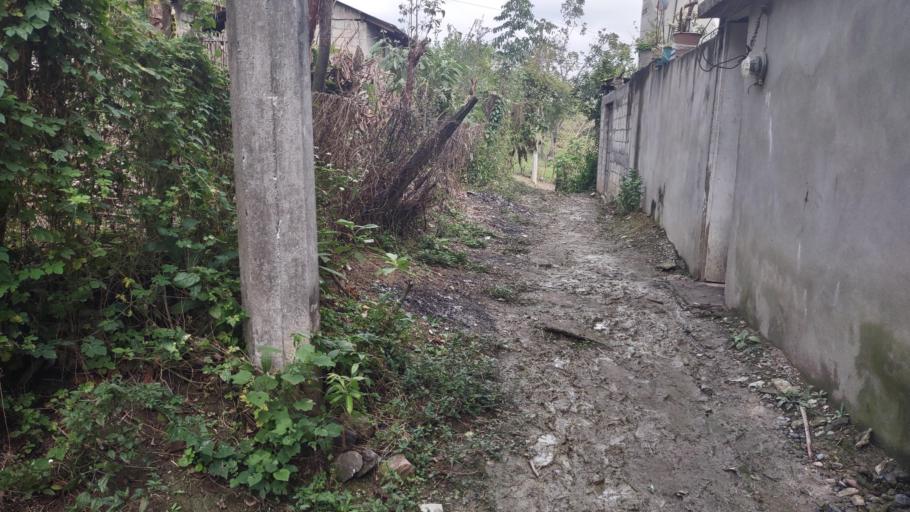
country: MX
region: Veracruz
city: Coatzintla
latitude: 20.4595
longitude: -97.4195
